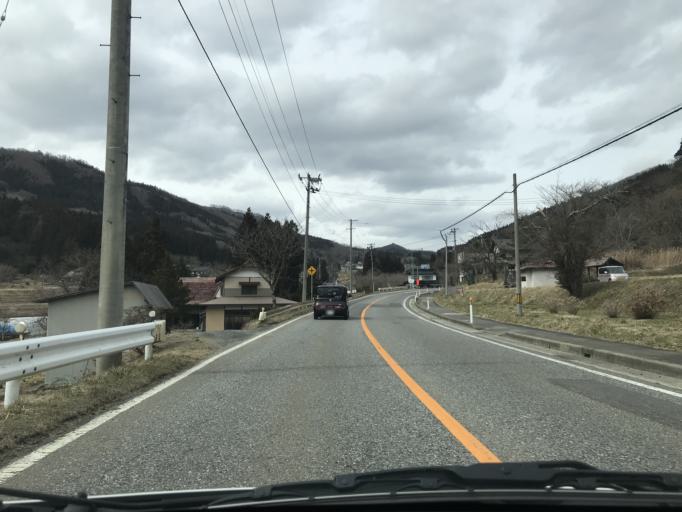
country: JP
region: Iwate
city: Tono
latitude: 39.3354
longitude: 141.4461
